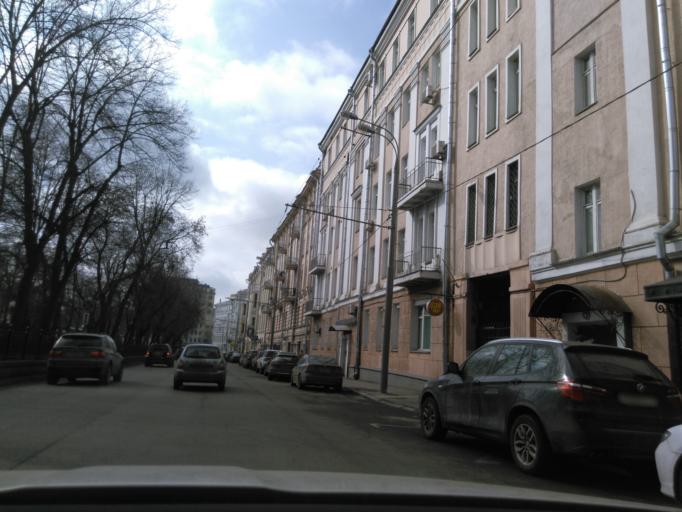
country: RU
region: Moscow
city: Moscow
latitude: 55.7487
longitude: 37.5995
